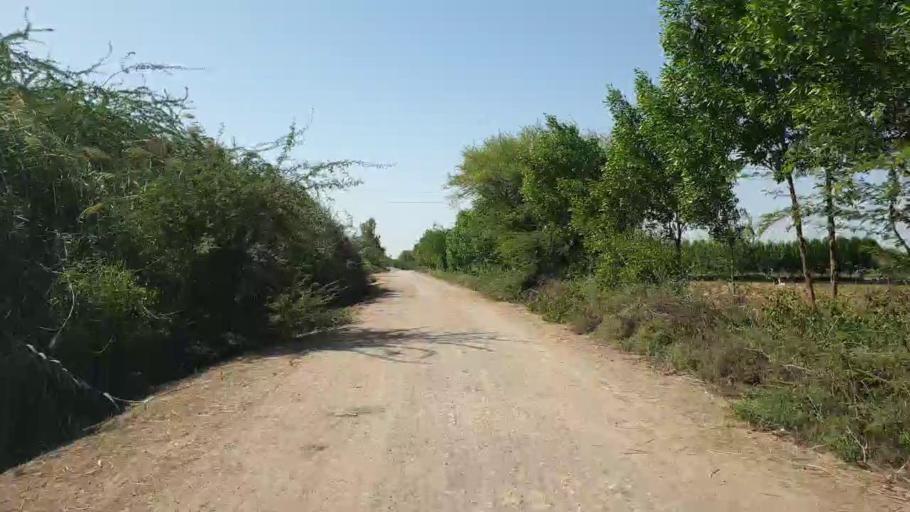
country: PK
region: Sindh
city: Tando Bago
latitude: 24.7048
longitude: 69.0258
